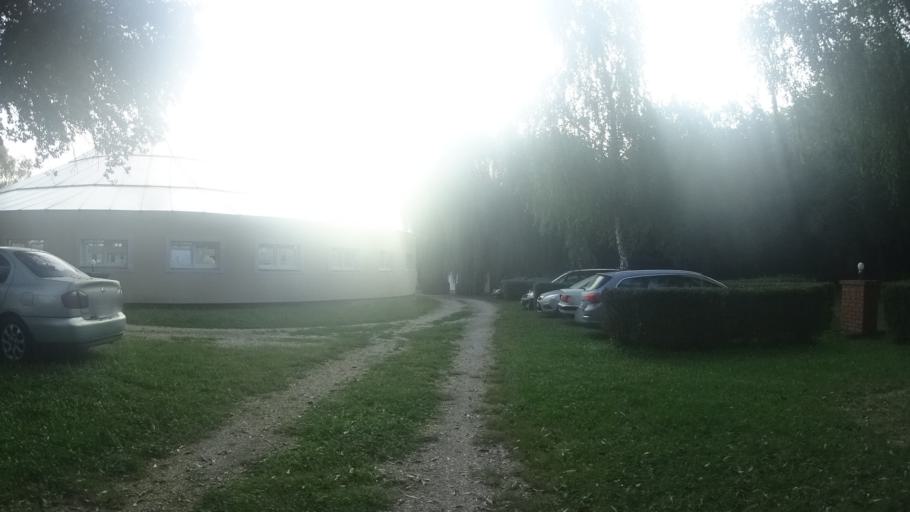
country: HU
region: Zala
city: Zalakomar
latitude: 46.5311
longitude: 17.1232
